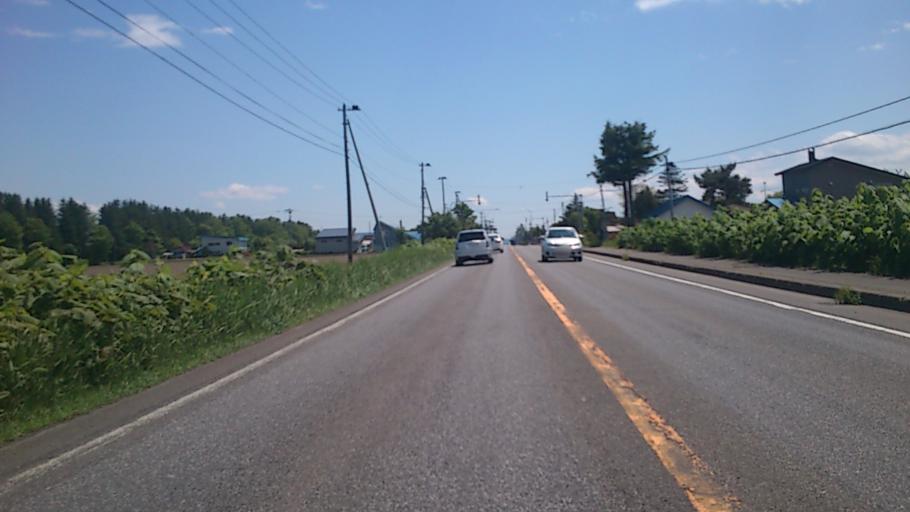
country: JP
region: Hokkaido
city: Nayoro
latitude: 44.2486
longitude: 142.3949
